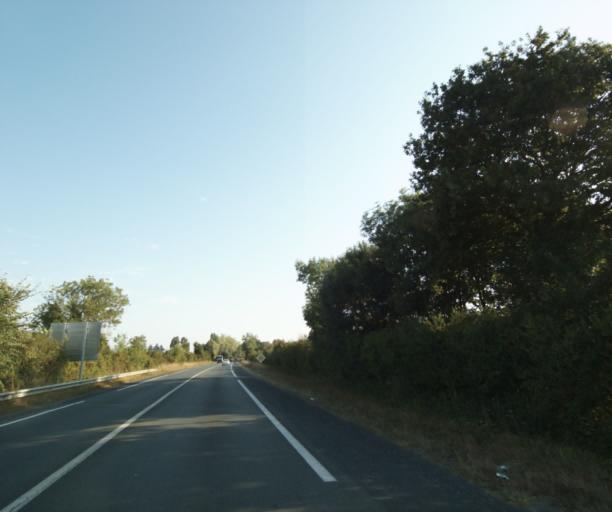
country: FR
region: Poitou-Charentes
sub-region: Departement de la Charente-Maritime
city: Saint-Hippolyte
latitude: 45.9192
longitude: -0.8856
